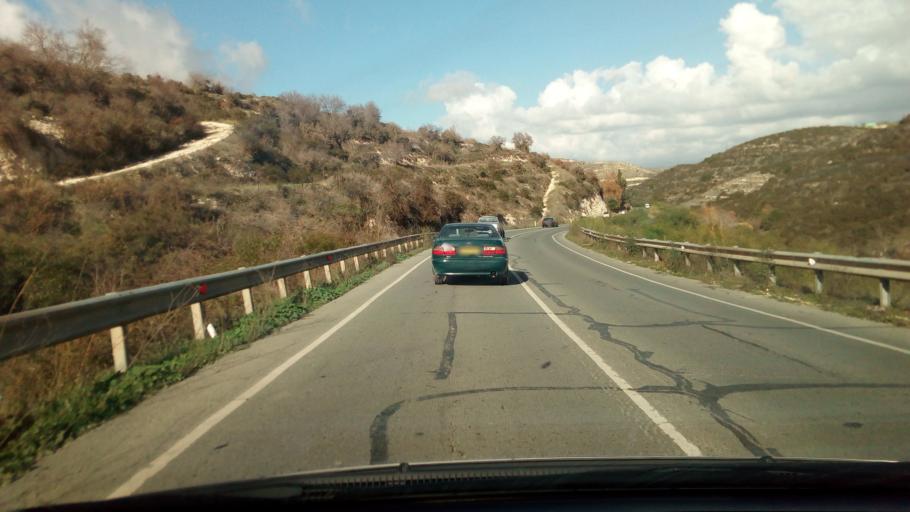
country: CY
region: Pafos
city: Mesogi
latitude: 34.8563
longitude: 32.4797
